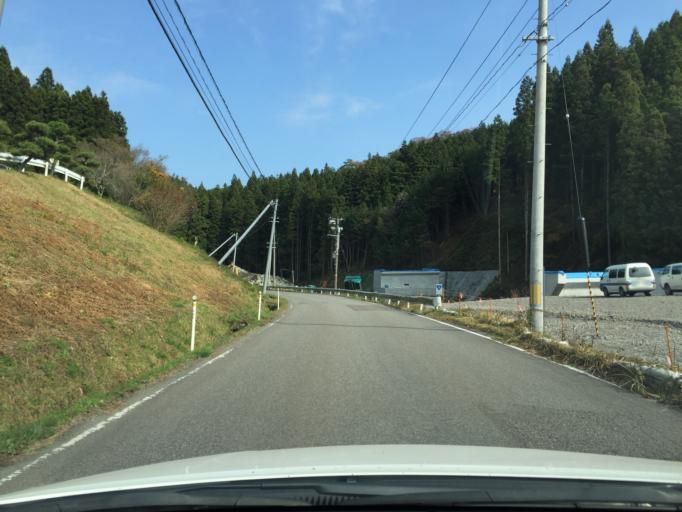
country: JP
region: Fukushima
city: Ishikawa
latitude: 36.9875
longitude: 140.4909
